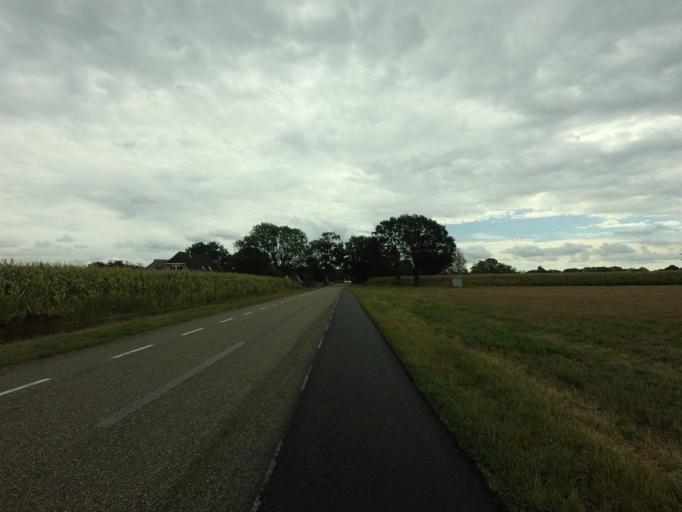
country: NL
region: Gelderland
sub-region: Gemeente Lochem
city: Laren
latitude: 52.2969
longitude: 6.3926
